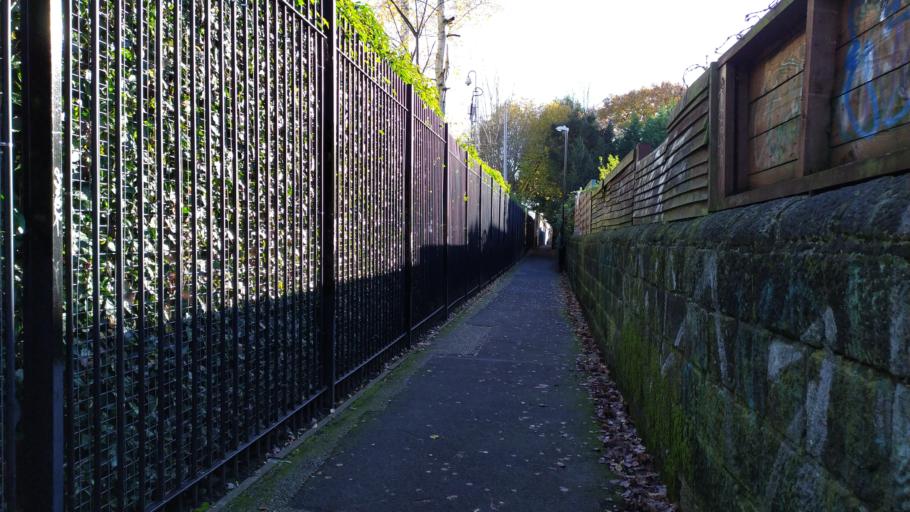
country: GB
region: England
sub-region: City and Borough of Leeds
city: Leeds
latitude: 53.8176
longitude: -1.5837
